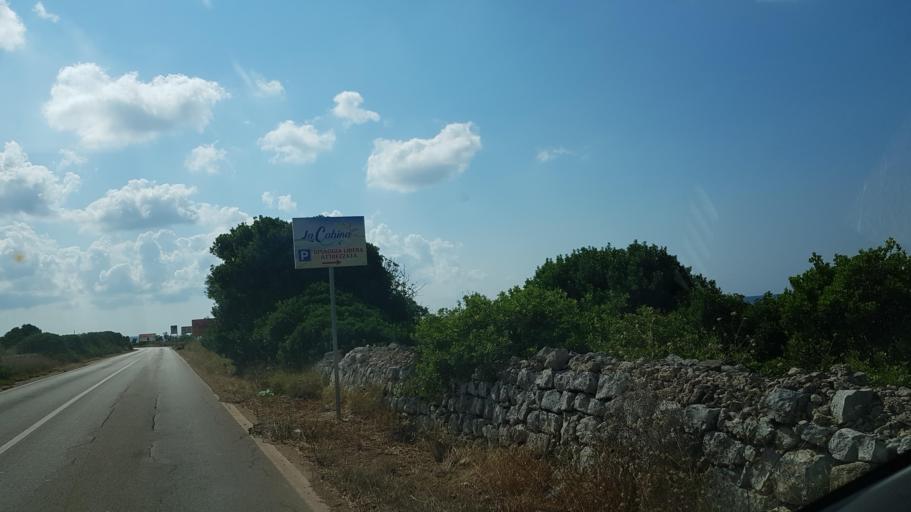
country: IT
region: Apulia
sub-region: Provincia di Lecce
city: Presicce
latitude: 39.8398
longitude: 18.2279
